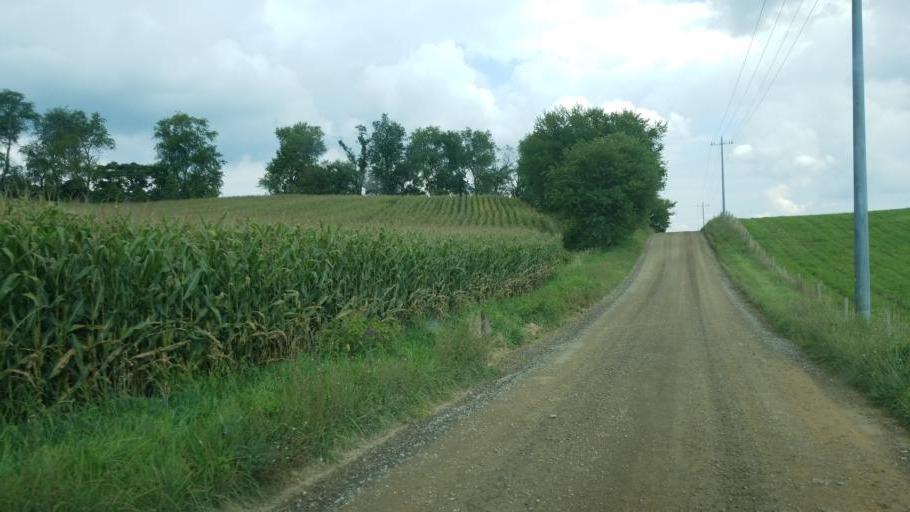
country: US
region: Ohio
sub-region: Knox County
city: Oak Hill
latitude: 40.4220
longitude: -82.2594
